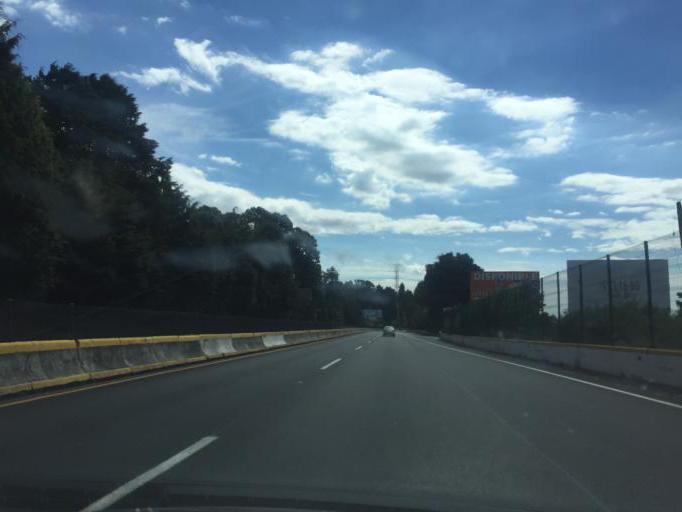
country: MX
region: Morelos
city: Tres Marias
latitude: 19.0486
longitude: -99.2395
